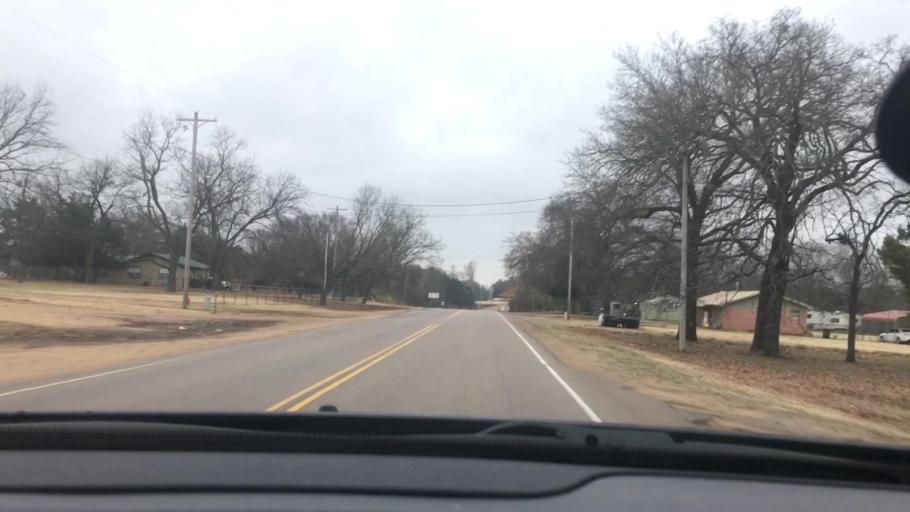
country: US
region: Oklahoma
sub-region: Johnston County
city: Tishomingo
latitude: 34.2492
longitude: -96.6711
